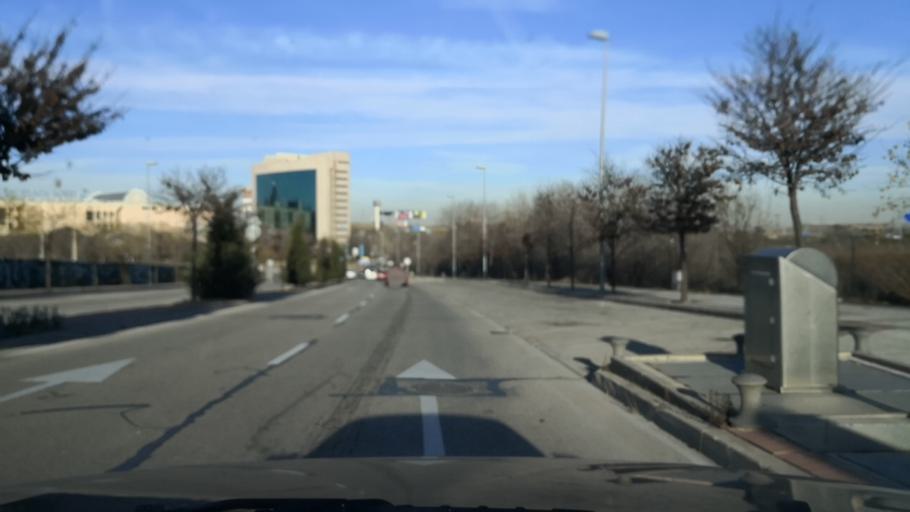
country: ES
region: Madrid
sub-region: Provincia de Madrid
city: San Sebastian de los Reyes
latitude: 40.5363
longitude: -3.6152
